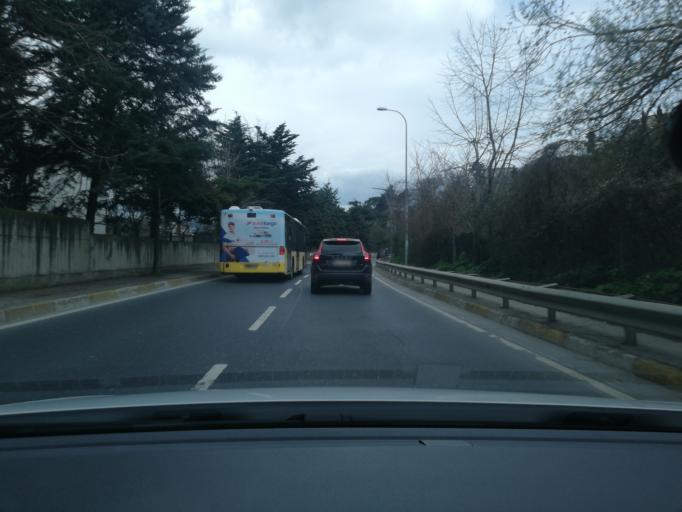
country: TR
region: Istanbul
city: UEskuedar
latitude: 41.0814
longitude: 29.0728
